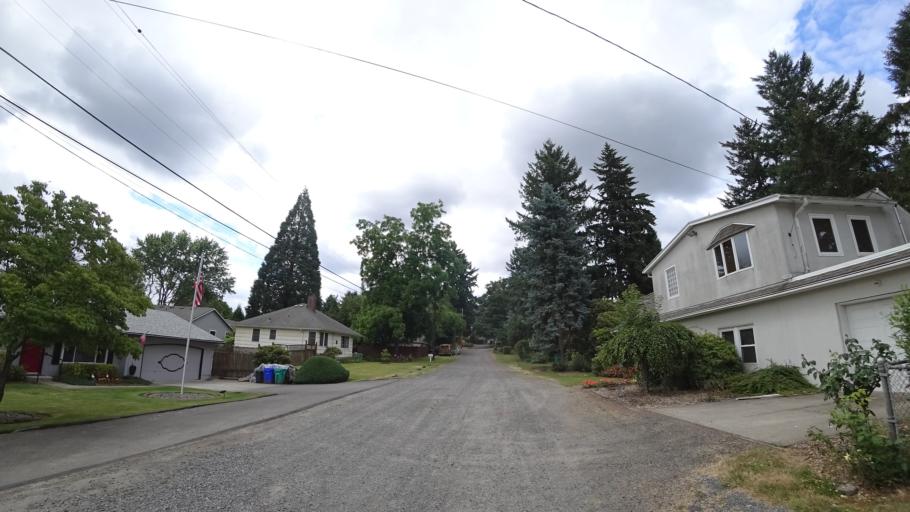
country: US
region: Oregon
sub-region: Multnomah County
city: Portland
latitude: 45.5660
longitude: -122.6117
